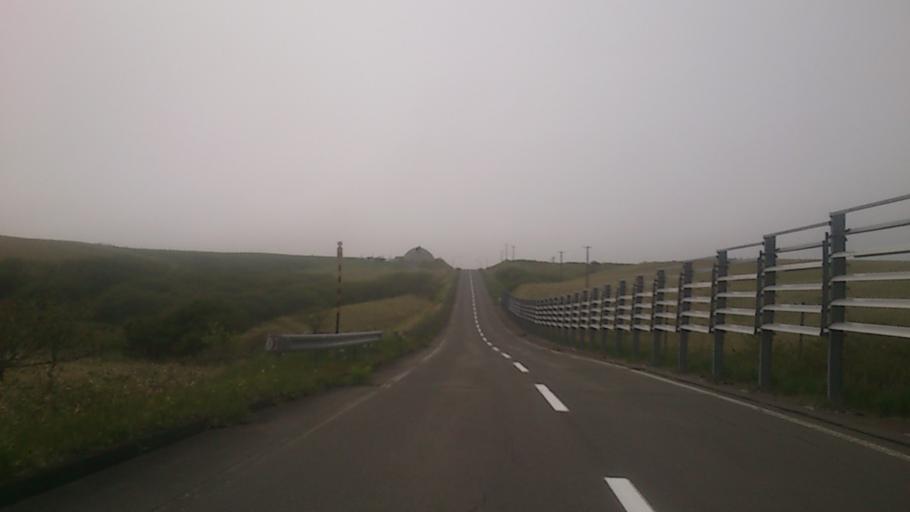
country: JP
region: Hokkaido
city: Nemuro
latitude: 43.1757
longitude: 145.3079
